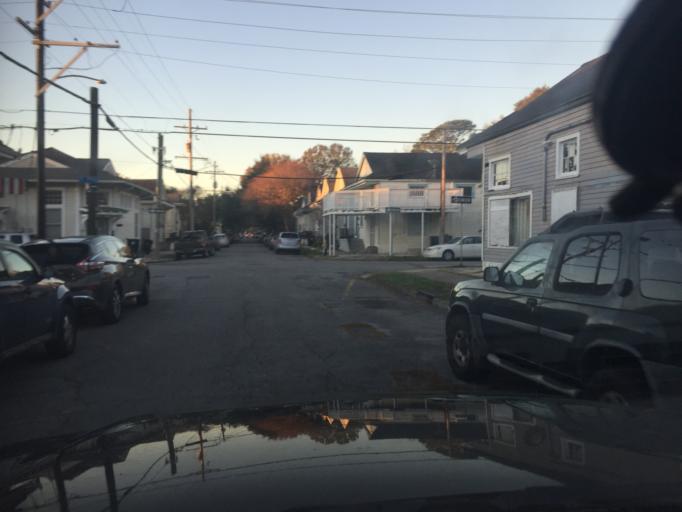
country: US
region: Louisiana
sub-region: Orleans Parish
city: New Orleans
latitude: 29.9776
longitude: -90.0869
